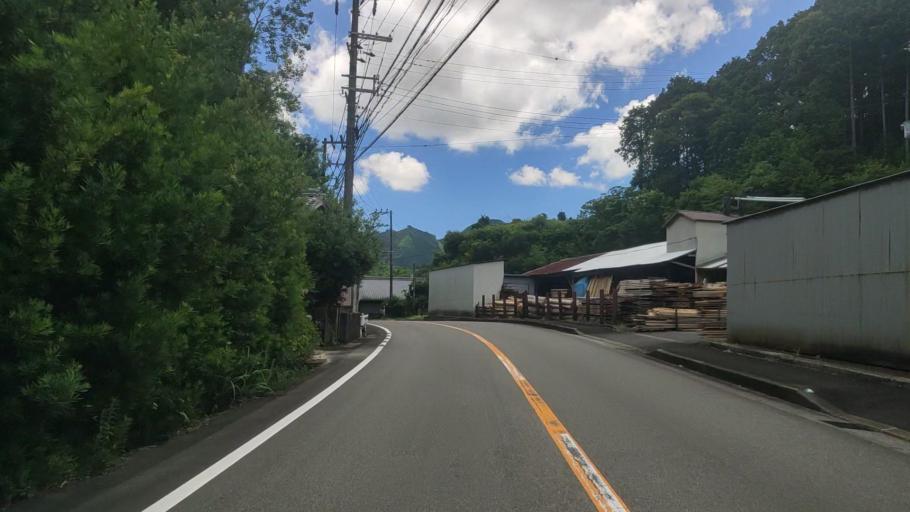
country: JP
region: Mie
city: Owase
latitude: 33.9508
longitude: 136.0698
